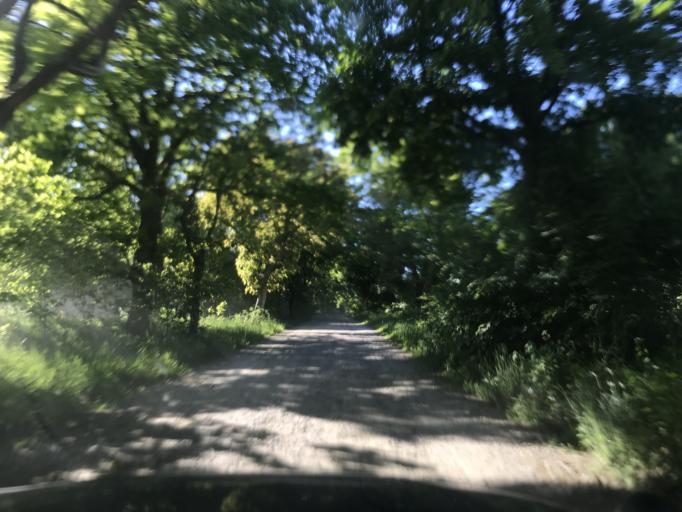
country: PL
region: West Pomeranian Voivodeship
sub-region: Powiat swidwinski
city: Polczyn-Zdroj
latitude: 53.7186
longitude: 16.1094
